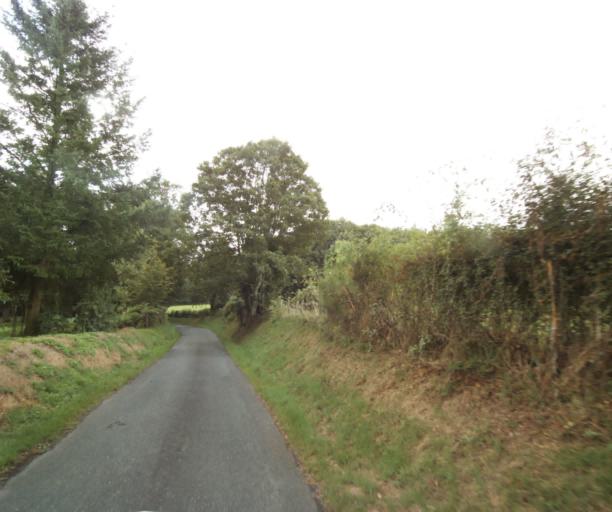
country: FR
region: Limousin
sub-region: Departement de la Correze
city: Sainte-Fortunade
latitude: 45.1933
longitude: 1.8041
